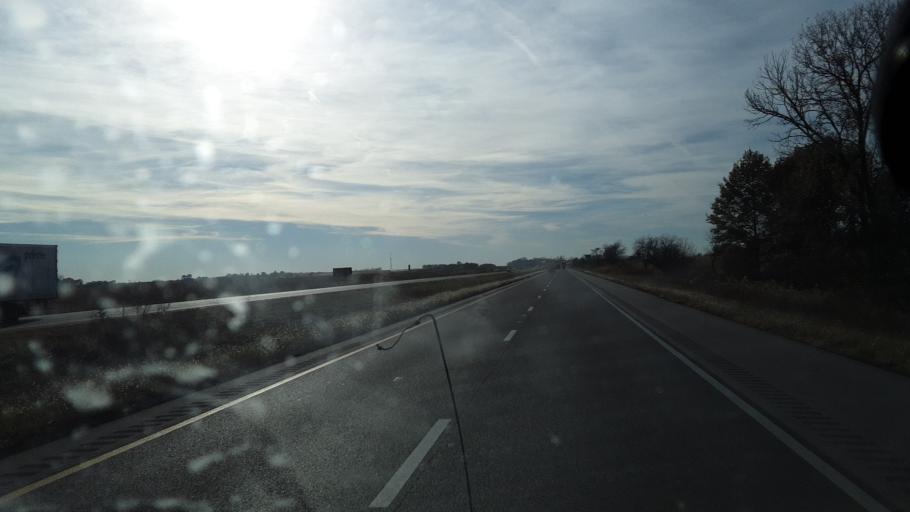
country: US
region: Illinois
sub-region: Bond County
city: Greenville
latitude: 38.8566
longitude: -89.4308
